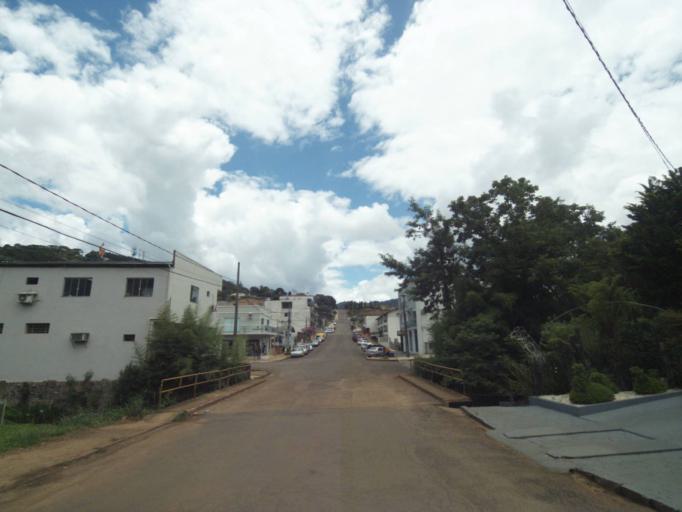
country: BR
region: Parana
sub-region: Uniao Da Vitoria
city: Uniao da Vitoria
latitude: -26.1586
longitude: -51.5532
